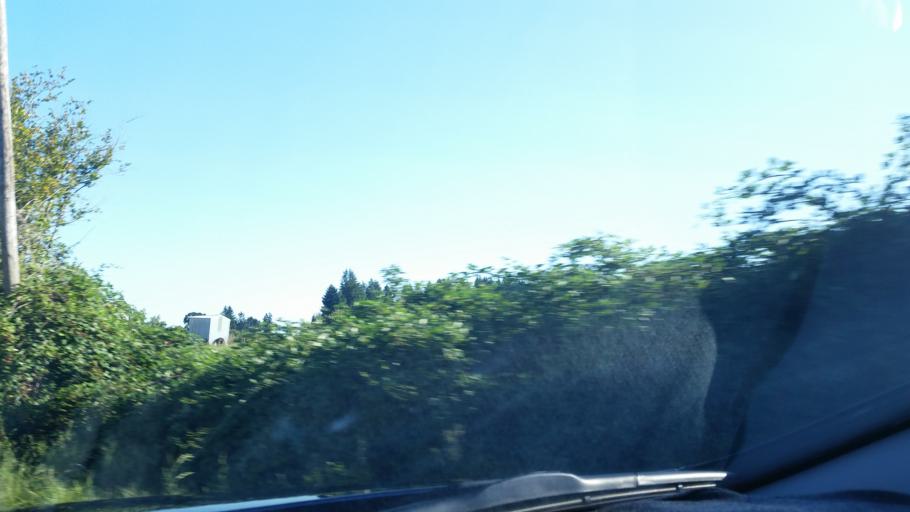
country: US
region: Oregon
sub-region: Marion County
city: Hubbard
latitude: 45.2439
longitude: -122.8740
